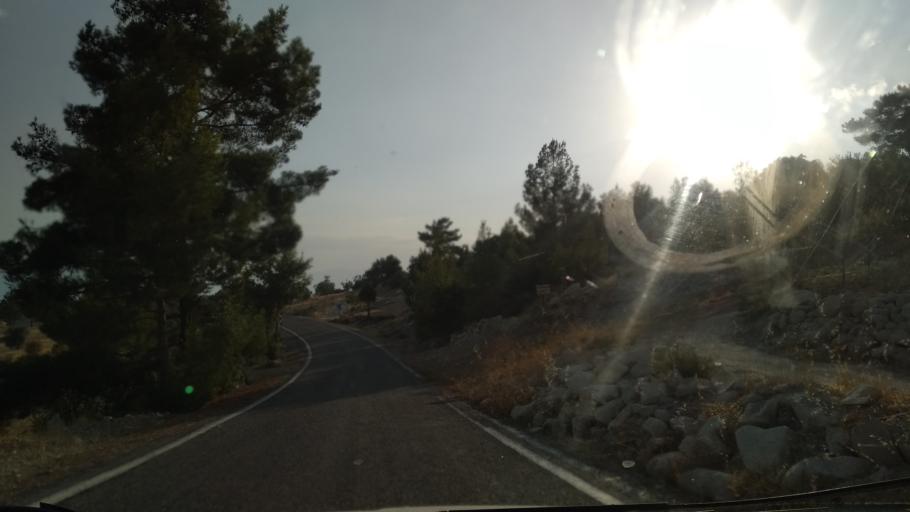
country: TR
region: Mersin
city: Sarikavak
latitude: 36.5627
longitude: 33.6294
